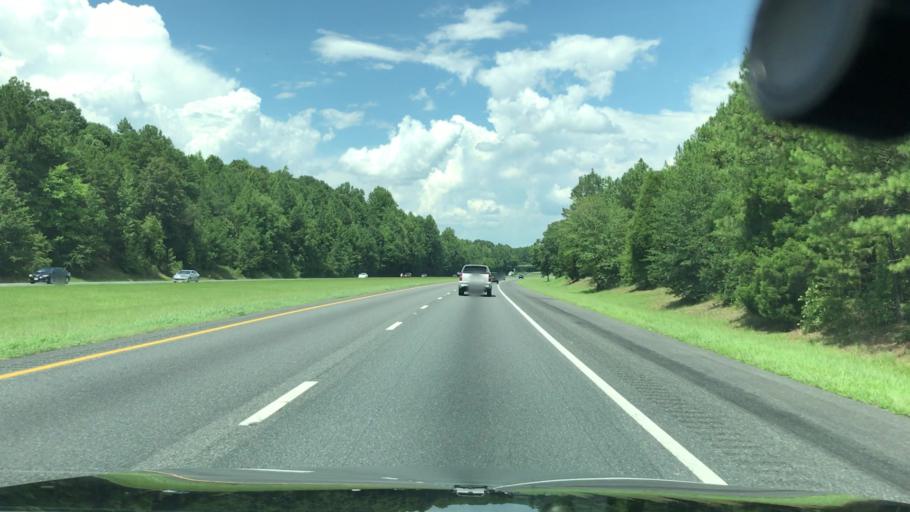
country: US
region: South Carolina
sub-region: York County
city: Rock Hill
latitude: 34.8265
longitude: -81.0319
